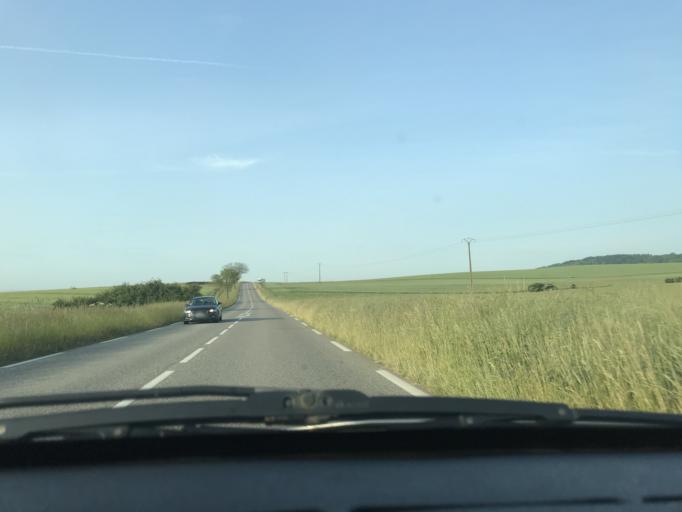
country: FR
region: Lorraine
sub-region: Departement de la Moselle
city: Chateau-Salins
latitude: 48.8714
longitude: 6.5328
